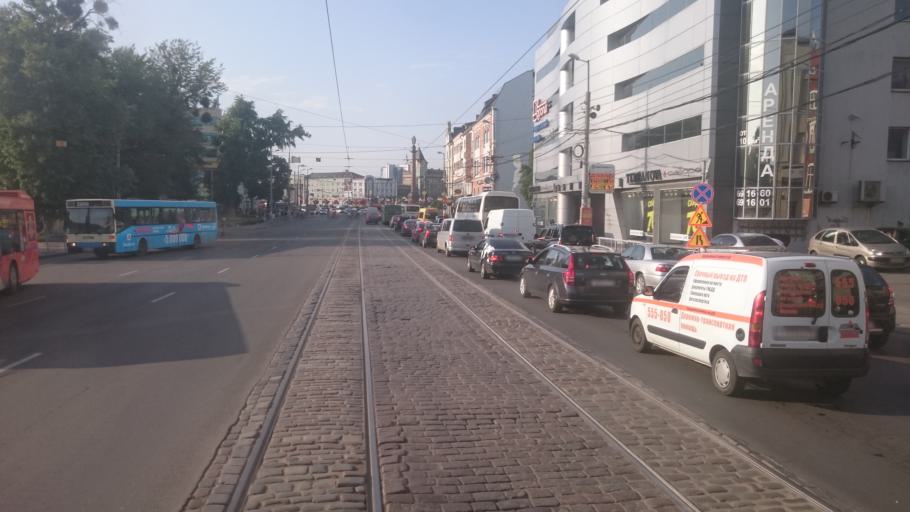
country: RU
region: Kaliningrad
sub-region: Gorod Kaliningrad
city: Kaliningrad
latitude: 54.7174
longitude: 20.5024
